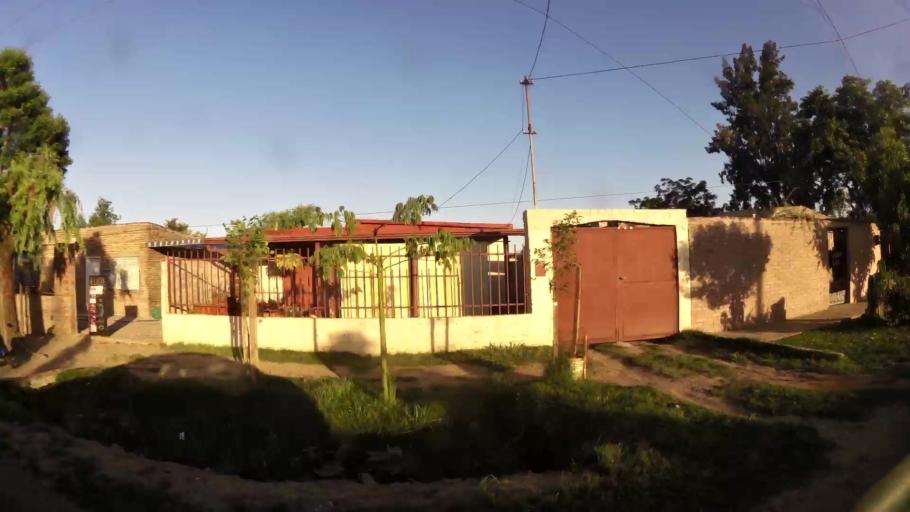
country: AR
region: Santa Fe
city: Santa Fe de la Vera Cruz
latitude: -31.5961
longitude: -60.6834
